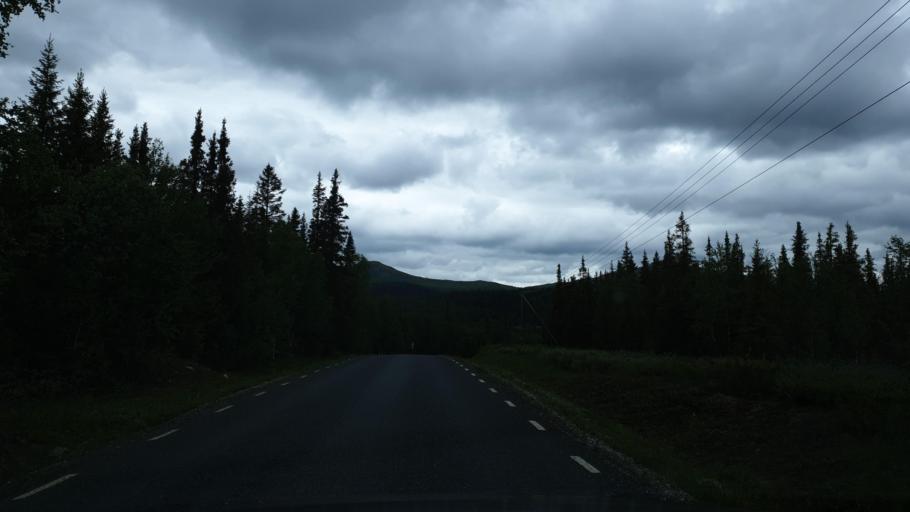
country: SE
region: Vaesterbotten
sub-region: Vilhelmina Kommun
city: Sjoberg
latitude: 65.2678
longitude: 15.3712
